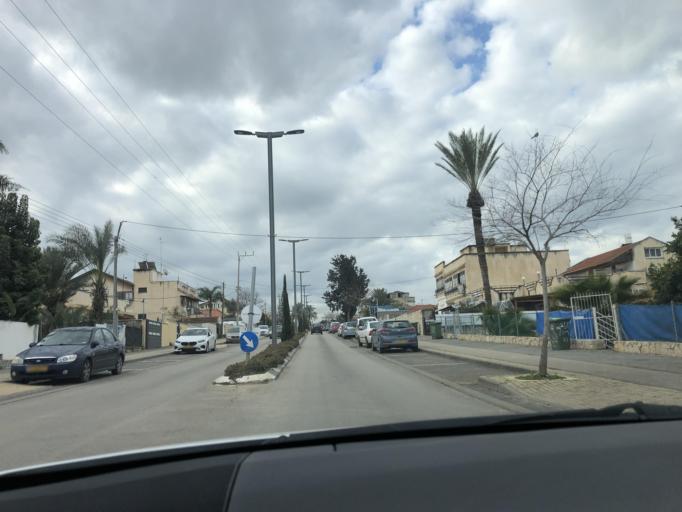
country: IL
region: Central District
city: Rosh Ha'Ayin
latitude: 32.0945
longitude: 34.9543
